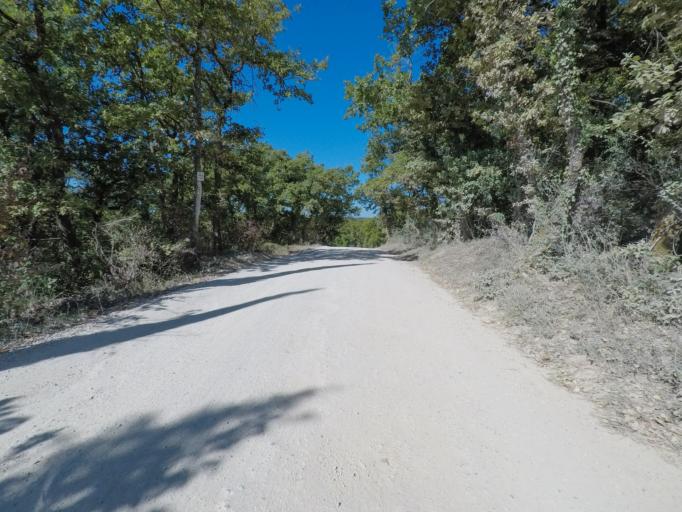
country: IT
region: Tuscany
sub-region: Provincia di Siena
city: Castellina in Chianti
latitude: 43.4389
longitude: 11.3106
